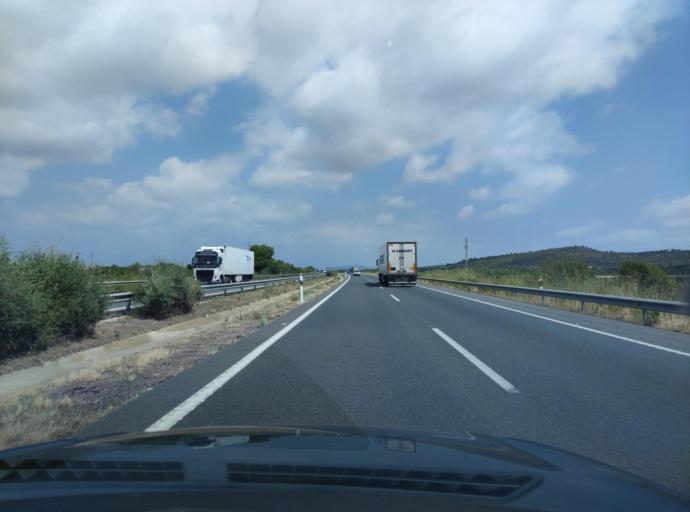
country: ES
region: Valencia
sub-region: Provincia de Castello
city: Vinaros
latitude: 40.4972
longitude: 0.4157
